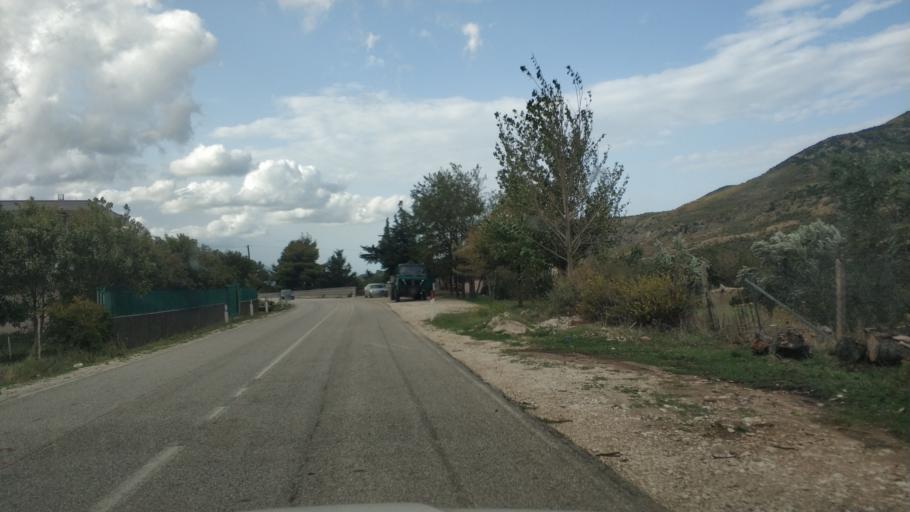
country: AL
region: Vlore
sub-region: Rrethi i Vlores
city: Orikum
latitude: 40.2715
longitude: 19.5127
